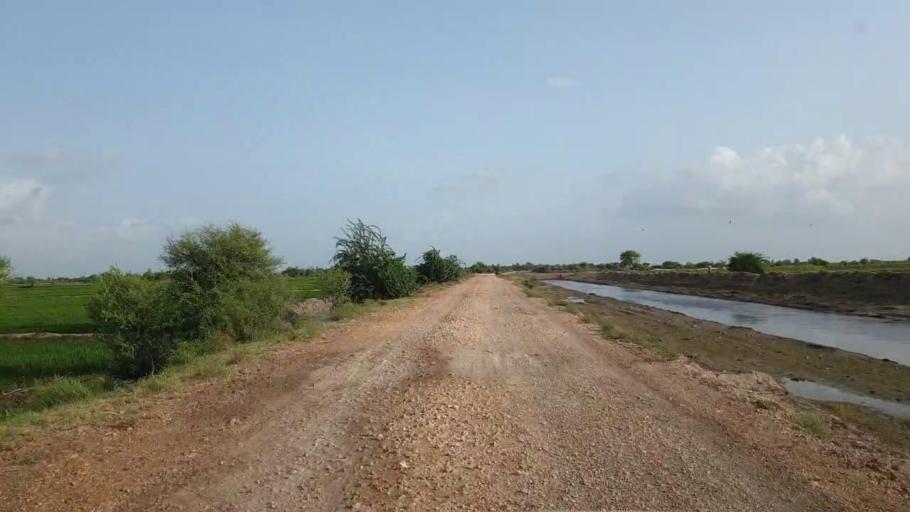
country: PK
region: Sindh
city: Kario
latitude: 24.8464
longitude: 68.6522
